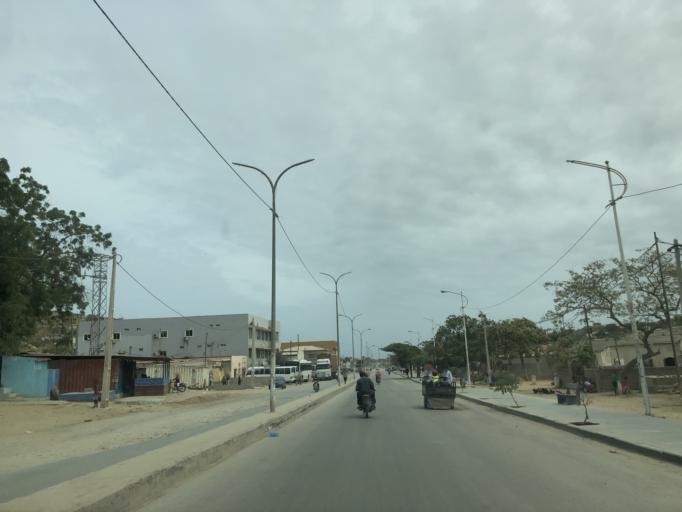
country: AO
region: Cuanza Sul
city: Sumbe
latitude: -11.2151
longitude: 13.8472
